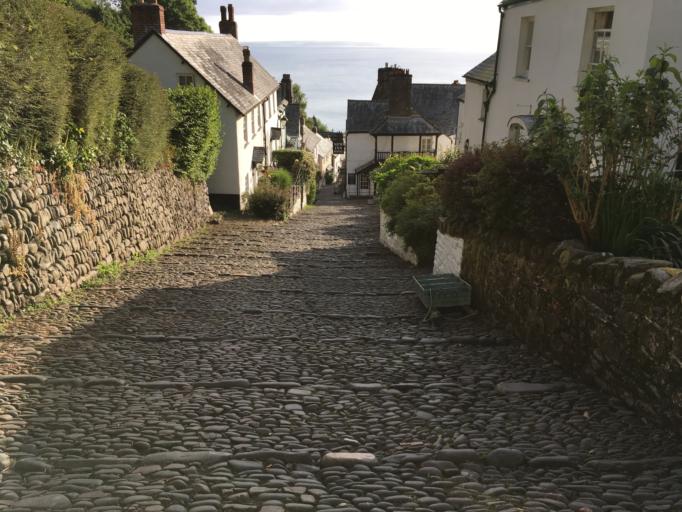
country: GB
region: England
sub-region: Devon
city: Northam
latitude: 50.9974
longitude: -4.4004
